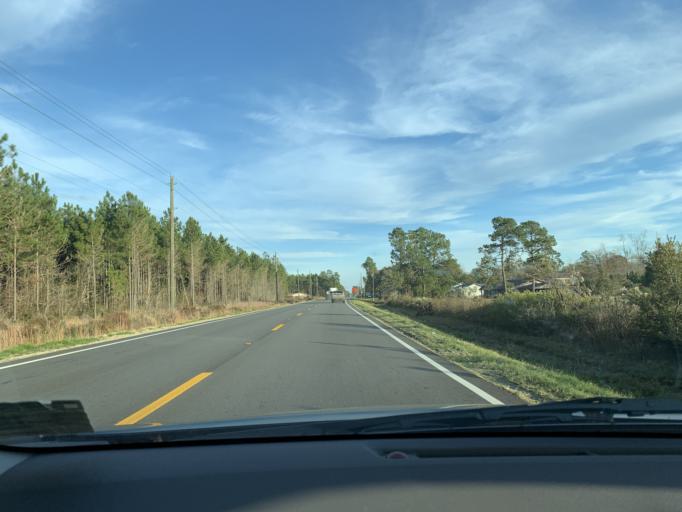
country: US
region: Georgia
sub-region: Irwin County
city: Ocilla
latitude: 31.5900
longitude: -83.0930
